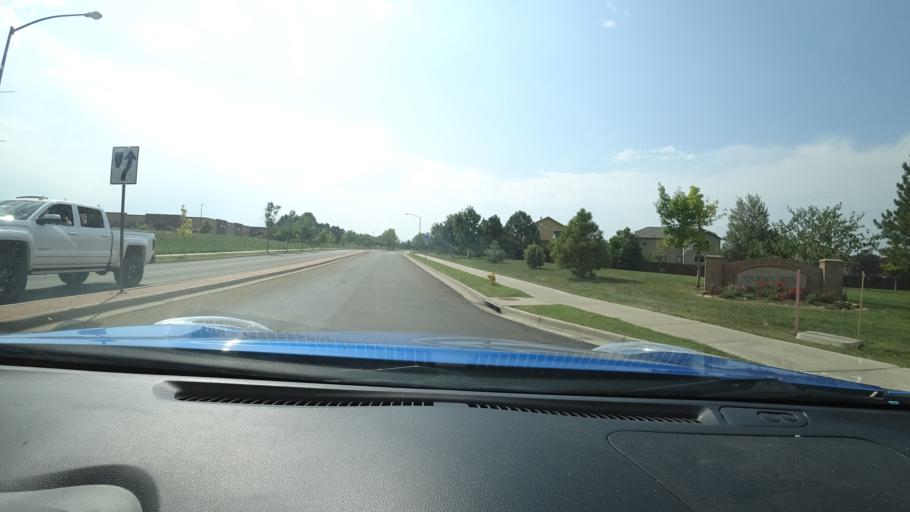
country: US
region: Colorado
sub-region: Adams County
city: Todd Creek
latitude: 39.9323
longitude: -104.9032
